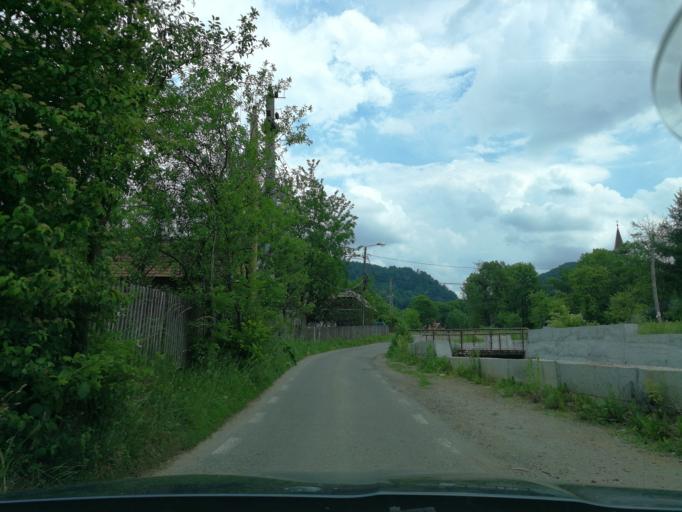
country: RO
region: Maramures
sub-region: Comuna Sisesti
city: Sisesti
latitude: 47.6195
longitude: 23.7300
